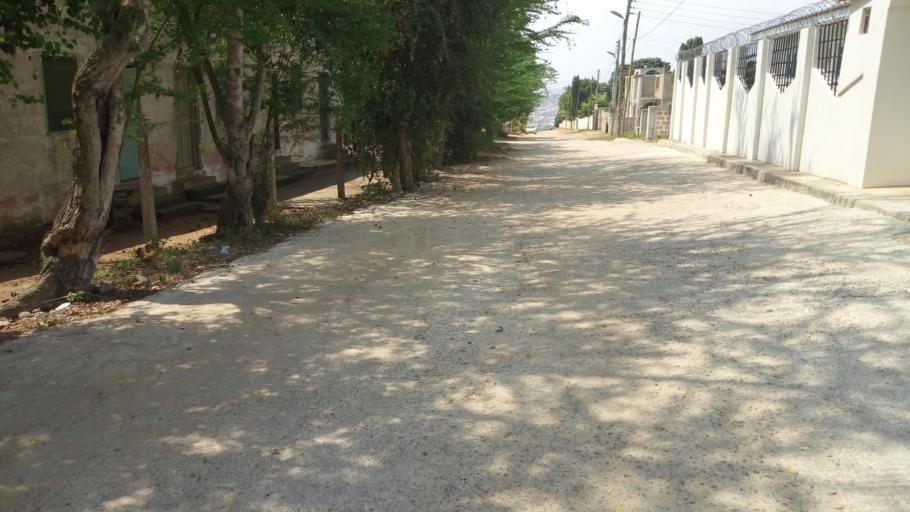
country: GH
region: Greater Accra
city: Gbawe
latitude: 5.5632
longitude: -0.3019
